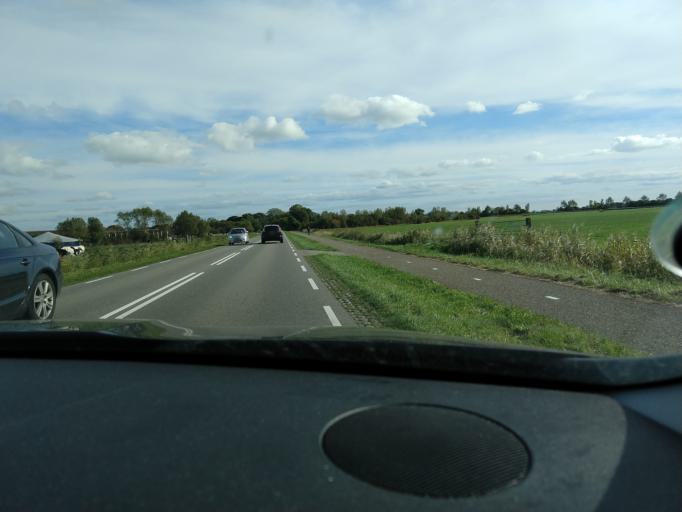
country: NL
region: Zeeland
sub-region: Gemeente Middelburg
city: Middelburg
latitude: 51.5364
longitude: 3.5522
